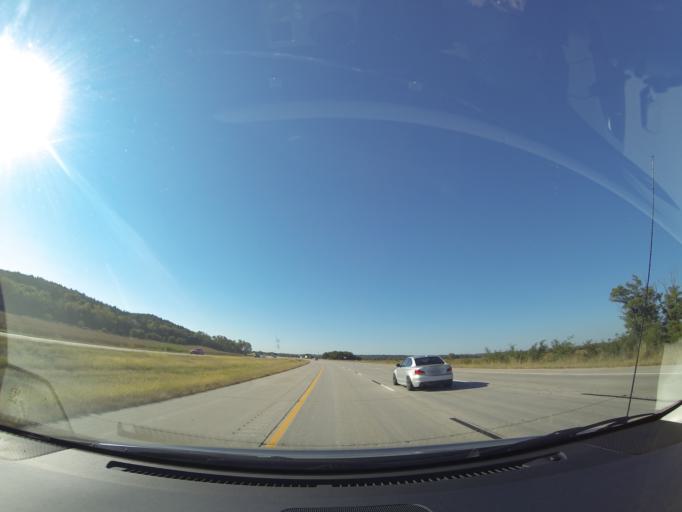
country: US
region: Nebraska
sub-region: Saunders County
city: Ashland
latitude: 41.0587
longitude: -96.2958
